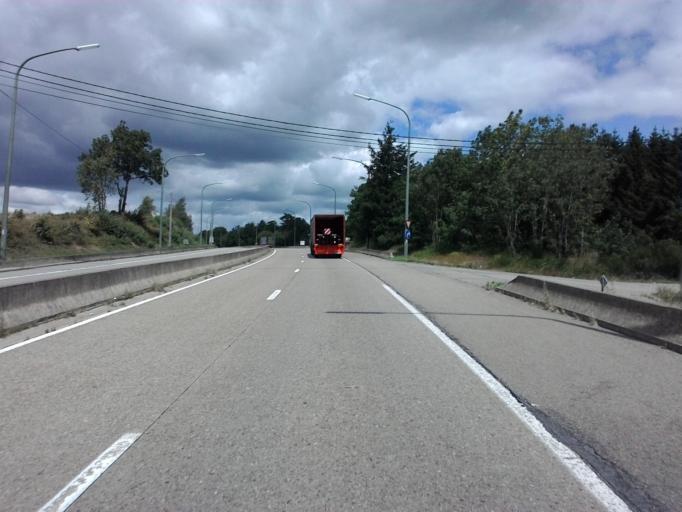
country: BE
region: Wallonia
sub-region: Province du Luxembourg
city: Martelange
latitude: 49.8527
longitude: 5.7325
